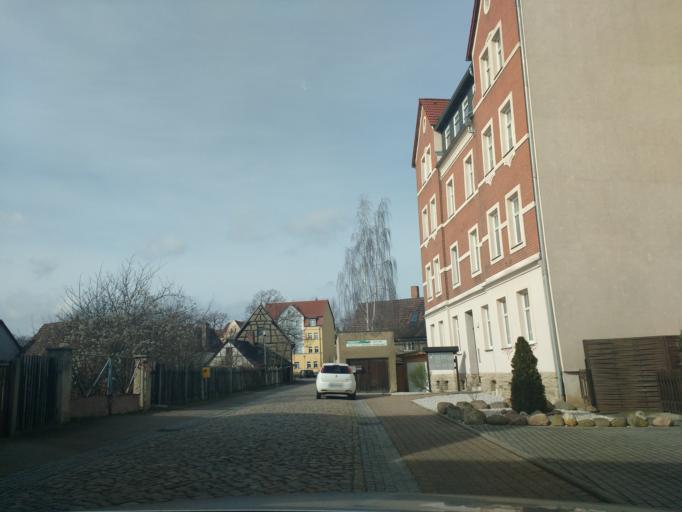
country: DE
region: Saxony-Anhalt
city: Zeitz
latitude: 51.0658
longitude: 12.1422
